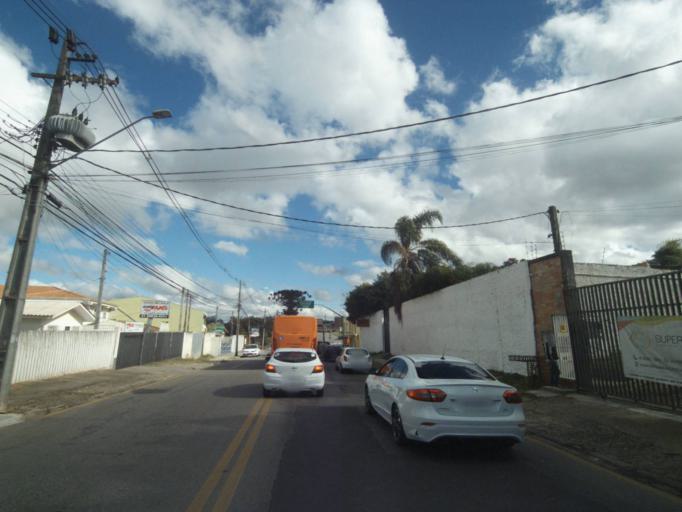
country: BR
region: Parana
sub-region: Sao Jose Dos Pinhais
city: Sao Jose dos Pinhais
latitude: -25.5230
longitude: -49.2928
